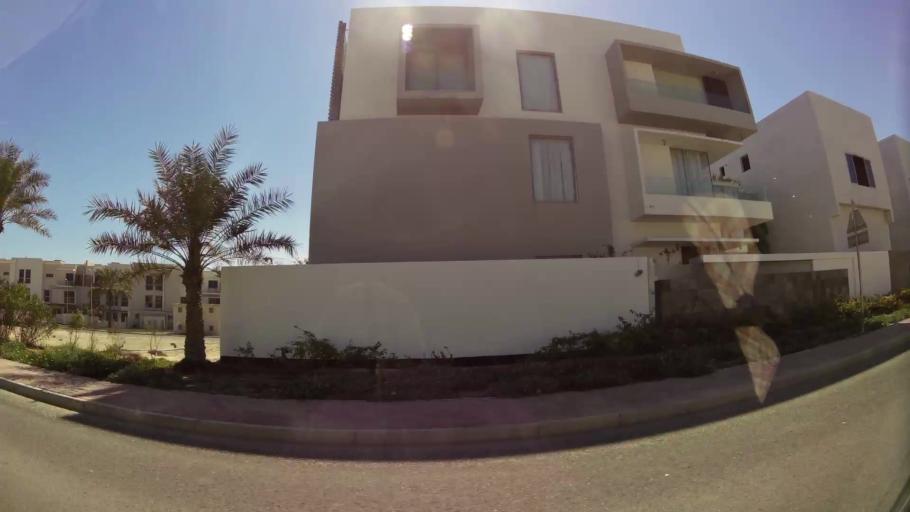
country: BH
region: Muharraq
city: Al Hadd
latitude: 26.2976
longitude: 50.6693
